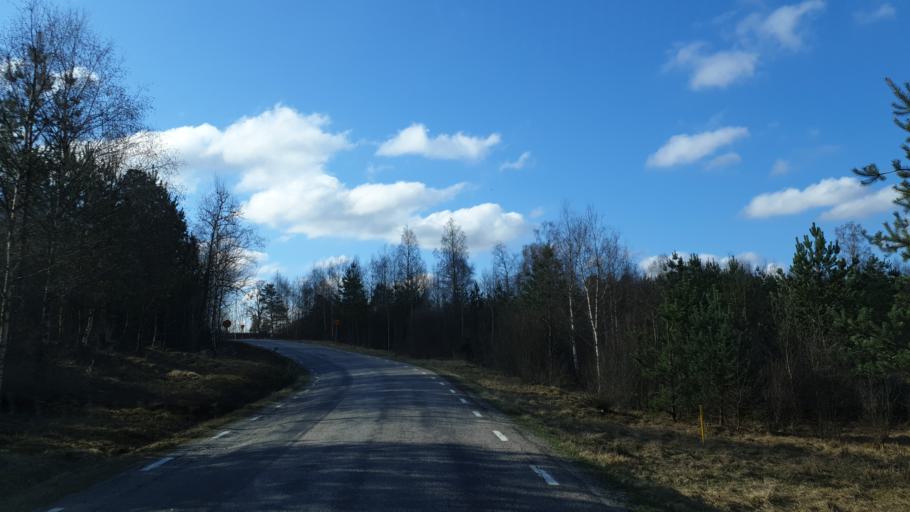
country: SE
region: Vaestra Goetaland
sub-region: Svenljunga Kommun
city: Svenljunga
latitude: 57.4438
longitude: 13.1195
